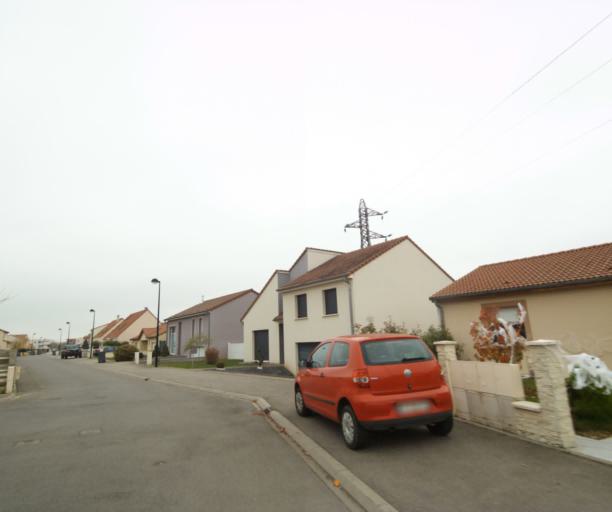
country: FR
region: Lorraine
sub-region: Departement de Meurthe-et-Moselle
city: Briey
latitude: 49.2417
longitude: 5.9335
